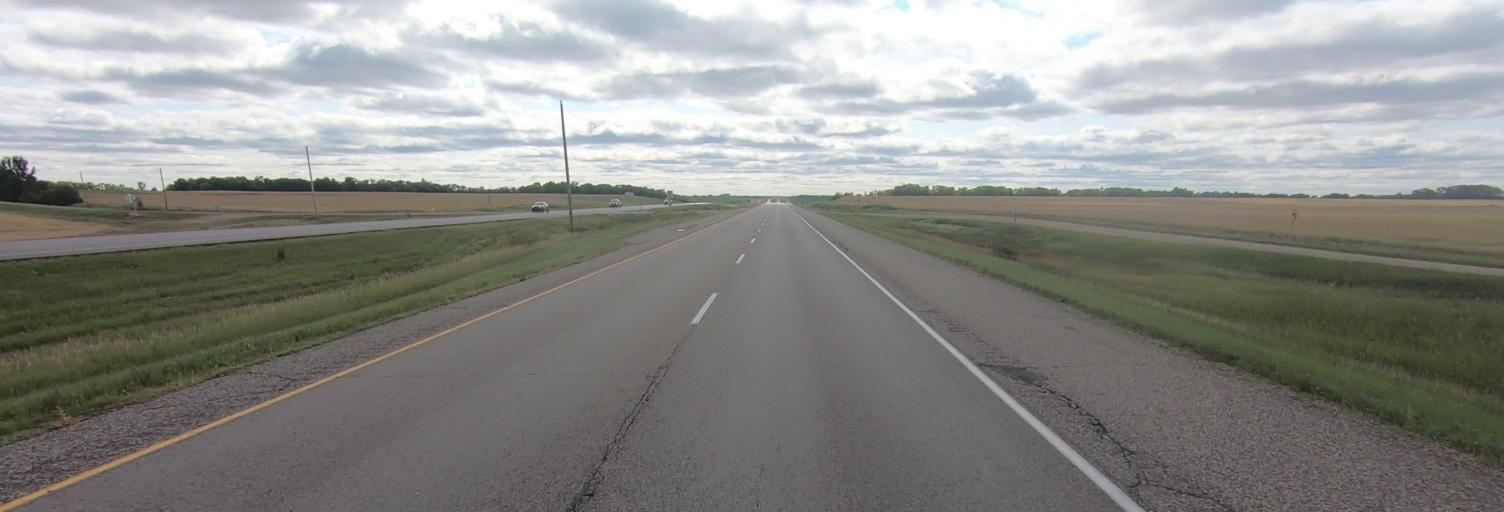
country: CA
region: Manitoba
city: Brandon
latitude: 49.8814
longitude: -100.0747
